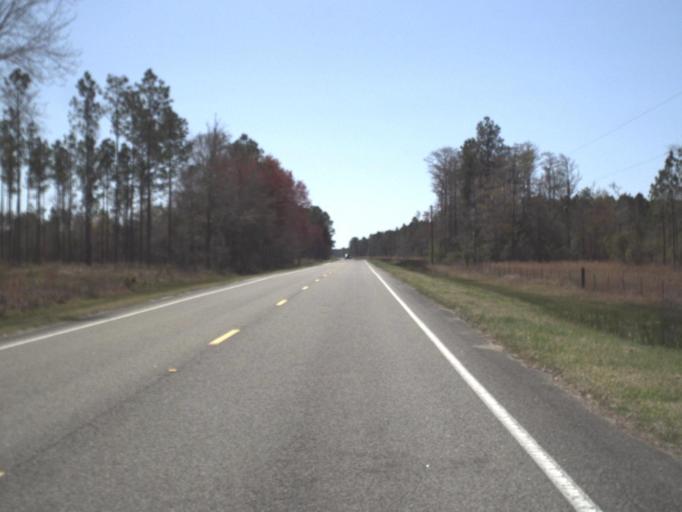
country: US
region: Florida
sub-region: Leon County
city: Woodville
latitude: 30.2553
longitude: -84.0426
